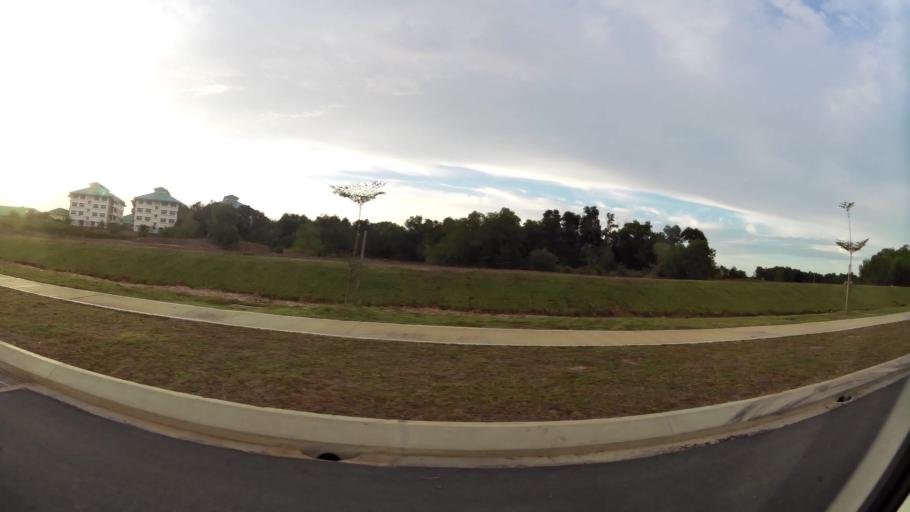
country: BN
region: Brunei and Muara
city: Bandar Seri Begawan
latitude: 4.9916
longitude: 114.9842
